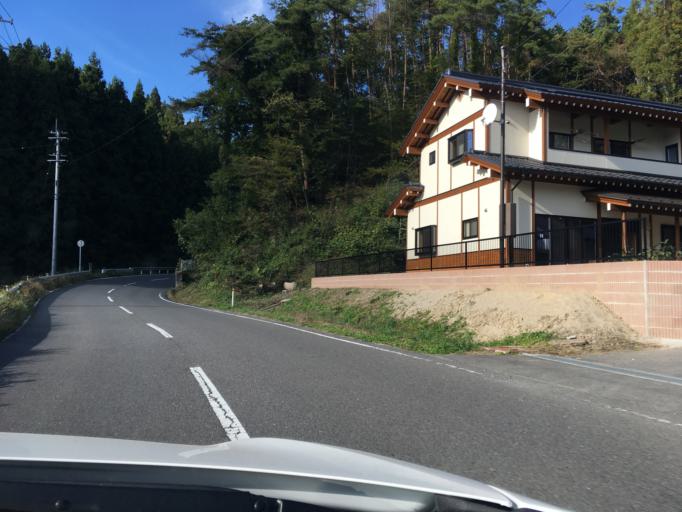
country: JP
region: Fukushima
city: Ishikawa
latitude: 37.1895
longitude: 140.4593
